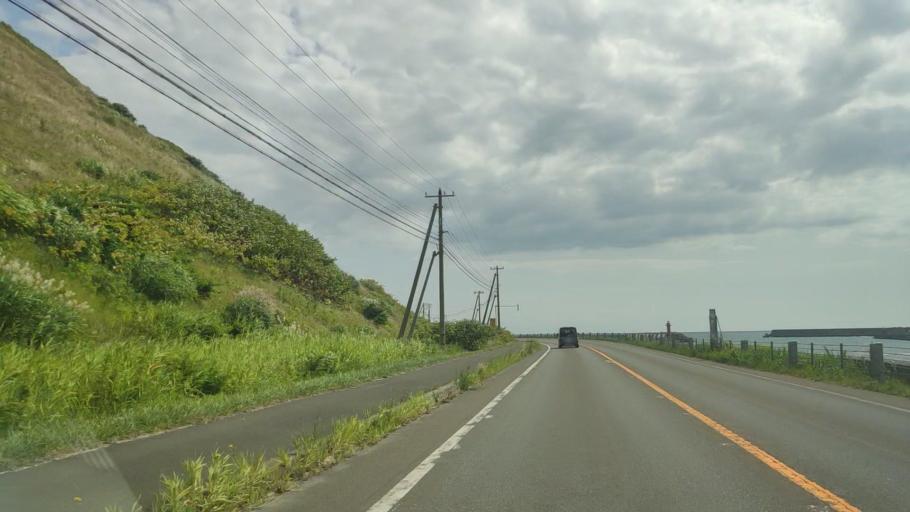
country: JP
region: Hokkaido
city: Rumoi
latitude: 44.2278
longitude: 141.6556
